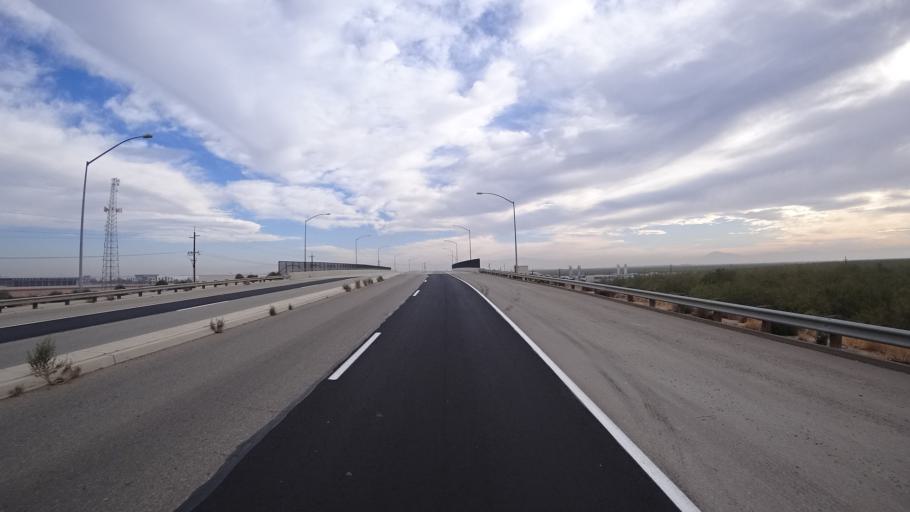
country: US
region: California
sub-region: Kern County
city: Rosedale
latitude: 35.4410
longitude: -119.2004
